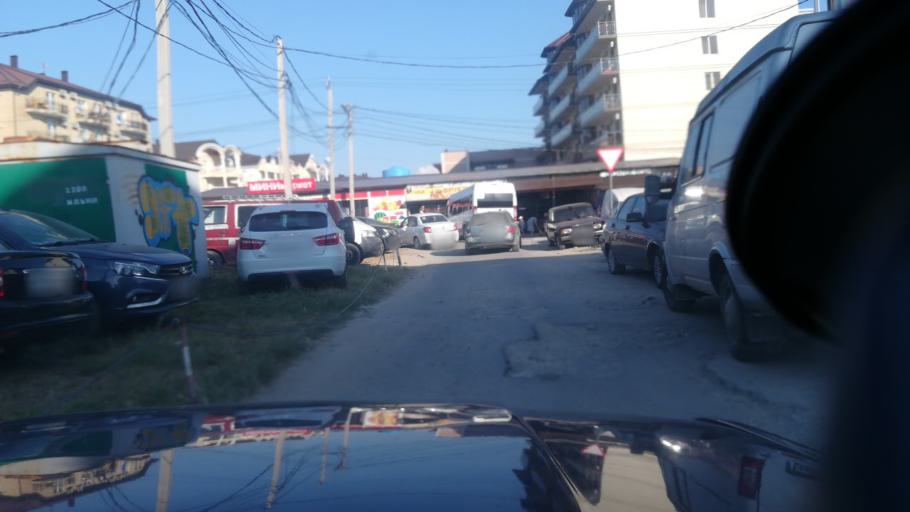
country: RU
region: Krasnodarskiy
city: Vityazevo
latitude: 44.9873
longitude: 37.2506
